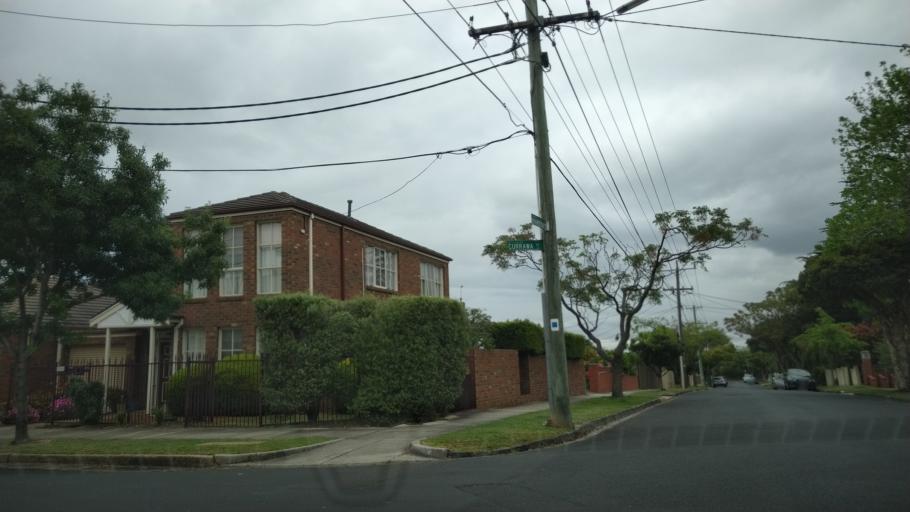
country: AU
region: Victoria
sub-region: Glen Eira
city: Caulfield
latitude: -37.8833
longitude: 145.0320
